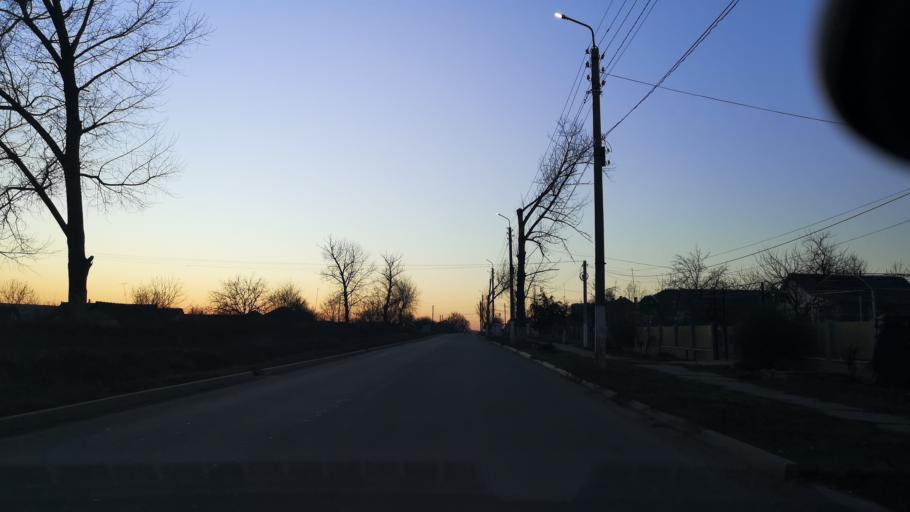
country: MD
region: Anenii Noi
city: Anenii Noi
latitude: 46.8899
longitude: 29.2862
